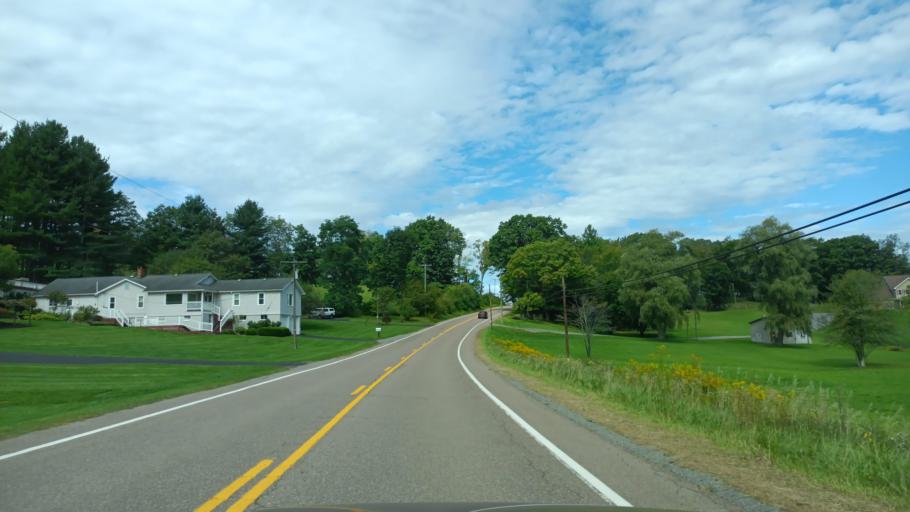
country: US
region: Maryland
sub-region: Garrett County
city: Oakland
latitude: 39.3028
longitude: -79.4470
